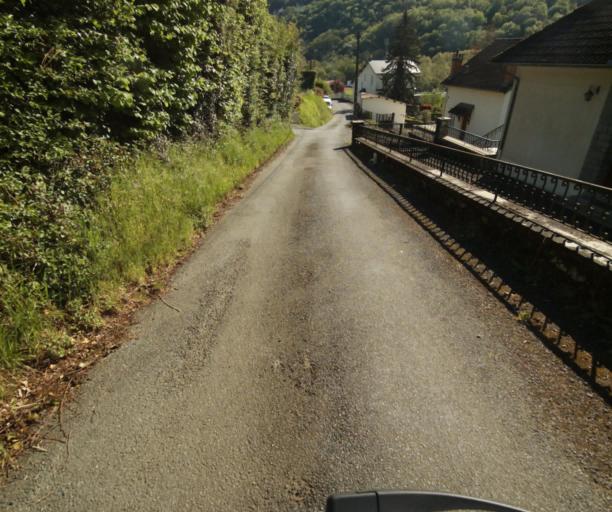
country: FR
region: Limousin
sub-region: Departement de la Correze
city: Tulle
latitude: 45.2773
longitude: 1.7799
